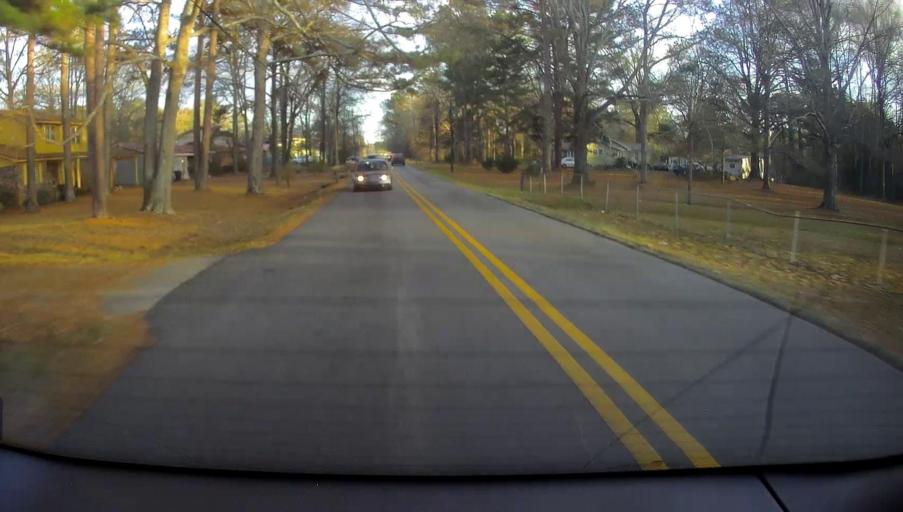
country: US
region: Alabama
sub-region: Etowah County
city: Glencoe
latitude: 33.9743
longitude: -85.9766
